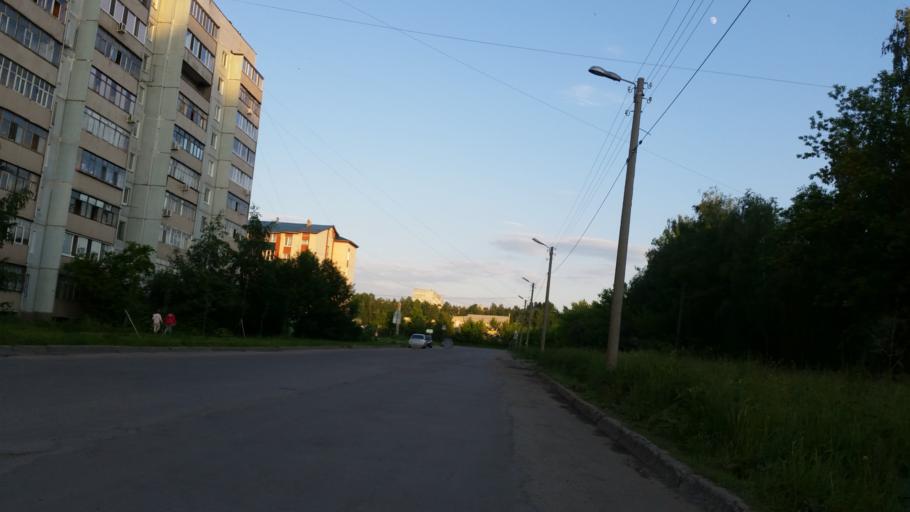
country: RU
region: Ulyanovsk
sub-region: Ulyanovskiy Rayon
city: Ulyanovsk
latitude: 54.3561
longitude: 48.3838
